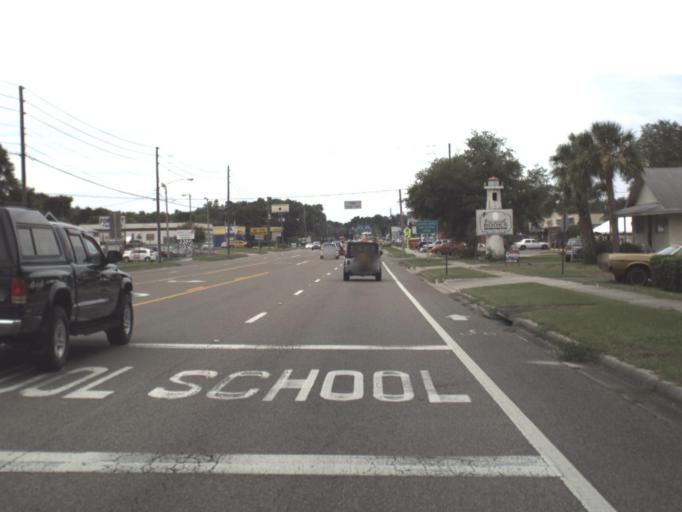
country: US
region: Florida
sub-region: Citrus County
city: Crystal River
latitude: 28.8986
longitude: -82.5796
